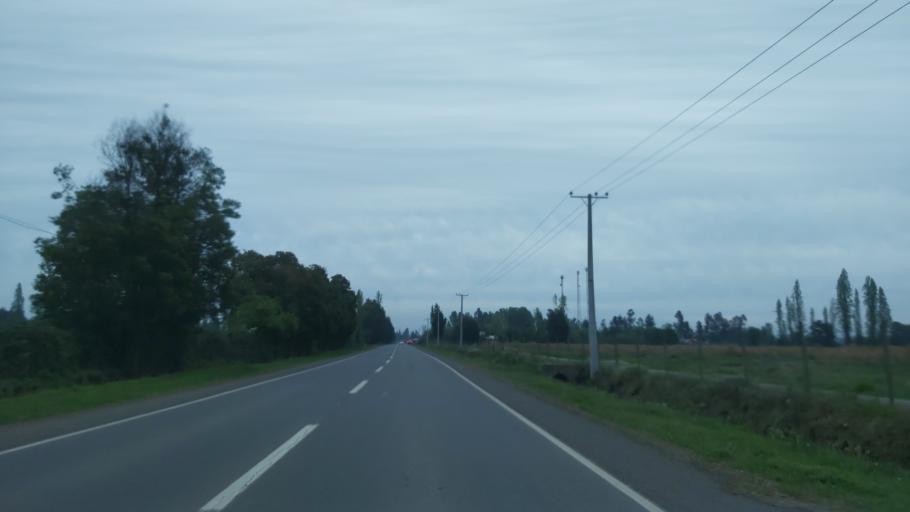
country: CL
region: Maule
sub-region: Provincia de Linares
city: Colbun
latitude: -35.7260
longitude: -71.4862
